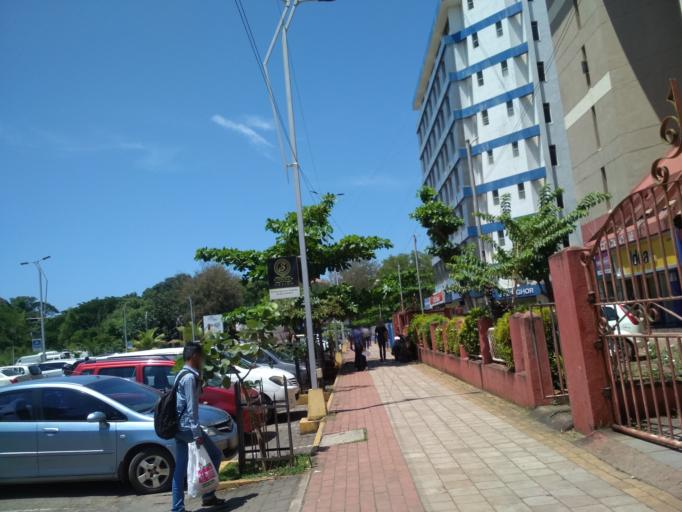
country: IN
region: Goa
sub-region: North Goa
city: Panaji
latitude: 15.4965
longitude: 73.8339
